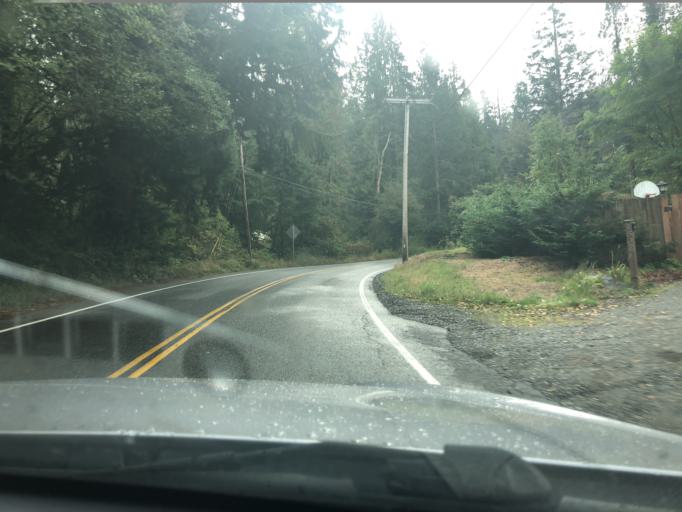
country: US
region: Washington
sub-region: King County
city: Riverbend
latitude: 47.4556
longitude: -121.7570
